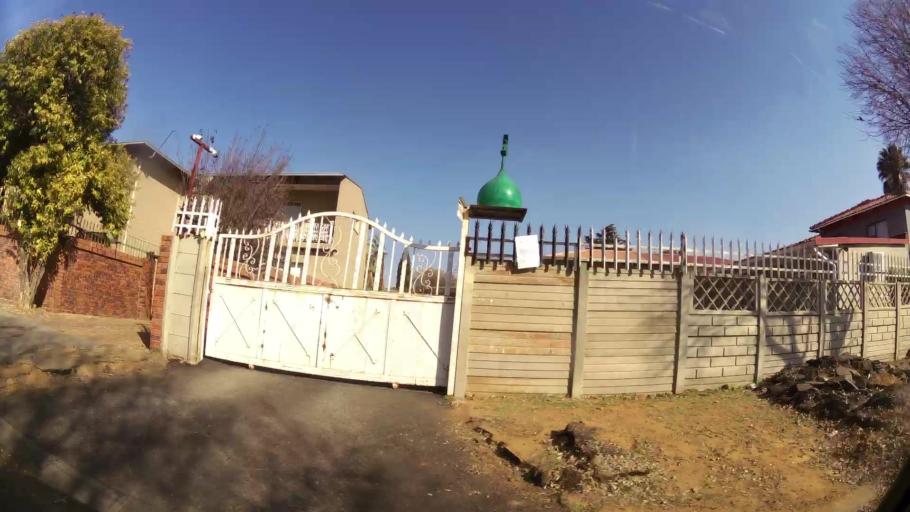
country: ZA
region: Gauteng
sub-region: City of Johannesburg Metropolitan Municipality
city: Johannesburg
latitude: -26.2494
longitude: 28.0055
